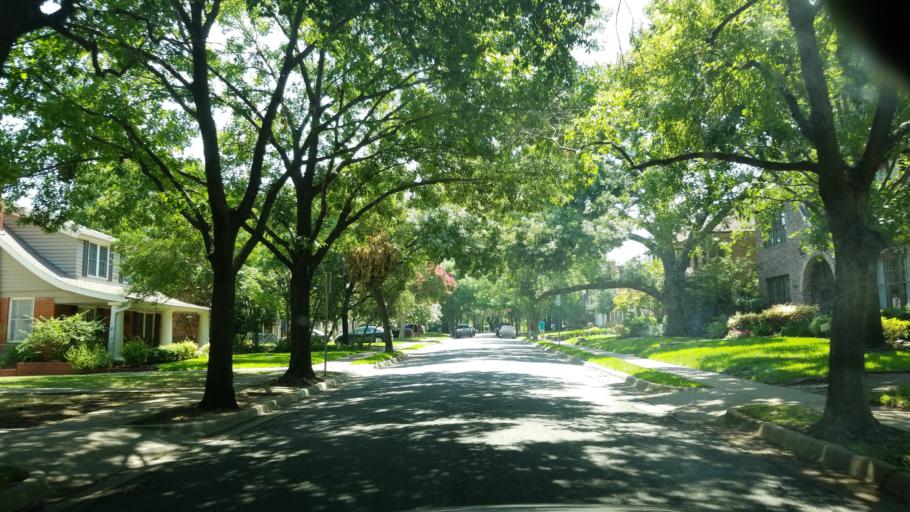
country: US
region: Texas
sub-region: Dallas County
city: University Park
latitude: 32.8484
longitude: -96.7843
